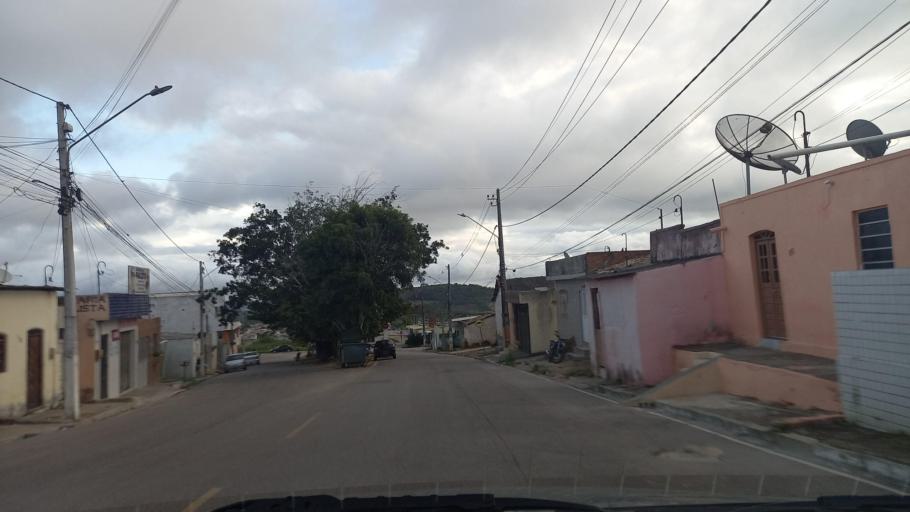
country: BR
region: Pernambuco
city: Garanhuns
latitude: -8.8838
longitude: -36.5055
